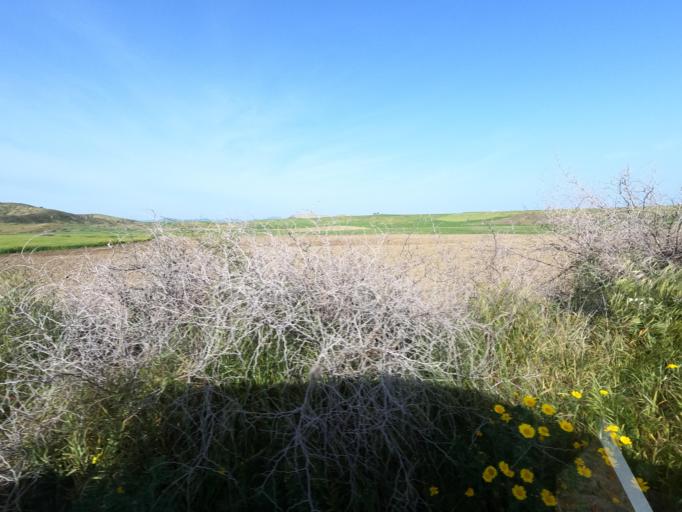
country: CY
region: Lefkosia
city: Lefka
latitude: 35.0914
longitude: 32.9443
